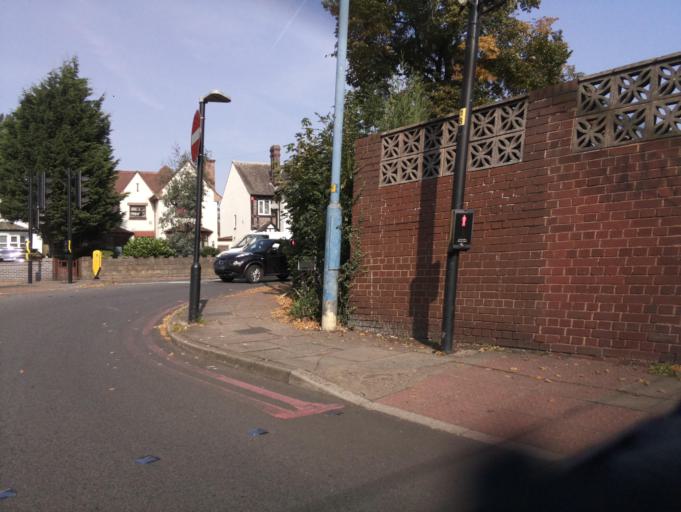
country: GB
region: England
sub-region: Sandwell
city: West Bromwich
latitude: 52.5350
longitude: -1.9846
